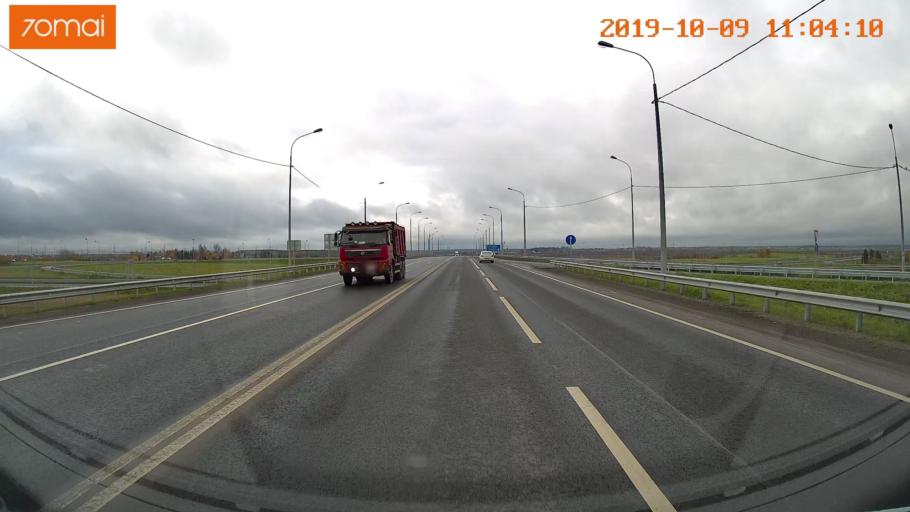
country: RU
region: Vologda
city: Vologda
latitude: 59.2148
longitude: 39.7703
